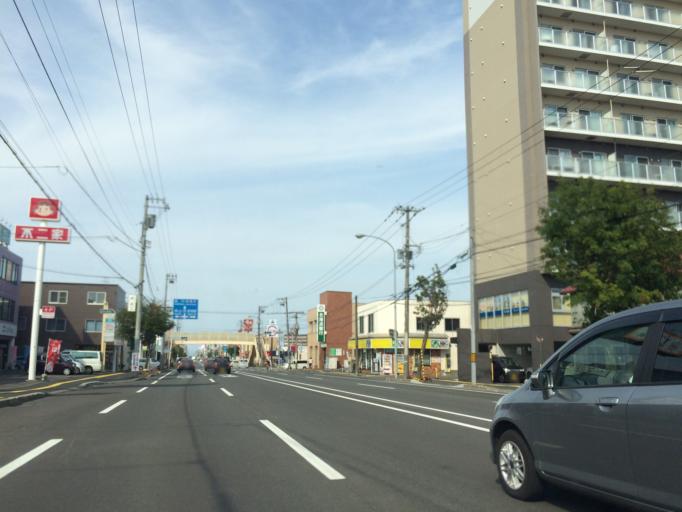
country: JP
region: Hokkaido
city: Ebetsu
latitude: 43.0928
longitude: 141.5232
